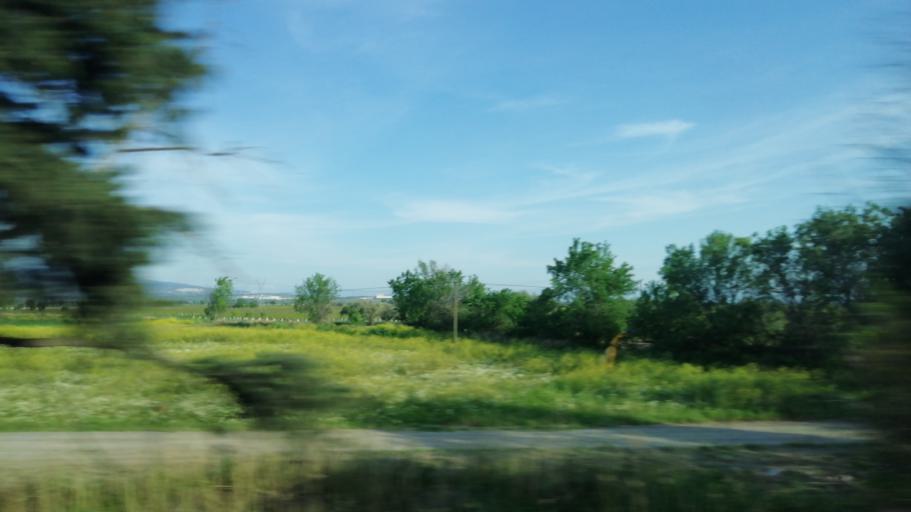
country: TR
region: Manisa
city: Saruhanli
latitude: 38.7198
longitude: 27.5599
